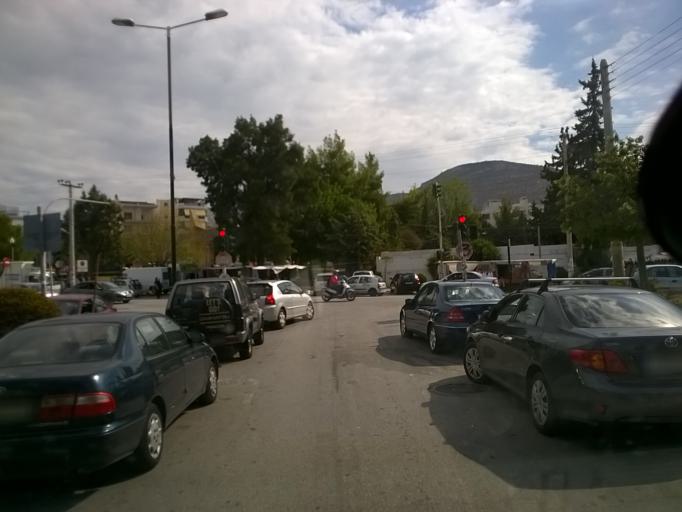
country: GR
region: Attica
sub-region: Nomarchia Athinas
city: Glyfada
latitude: 37.8849
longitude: 23.7595
